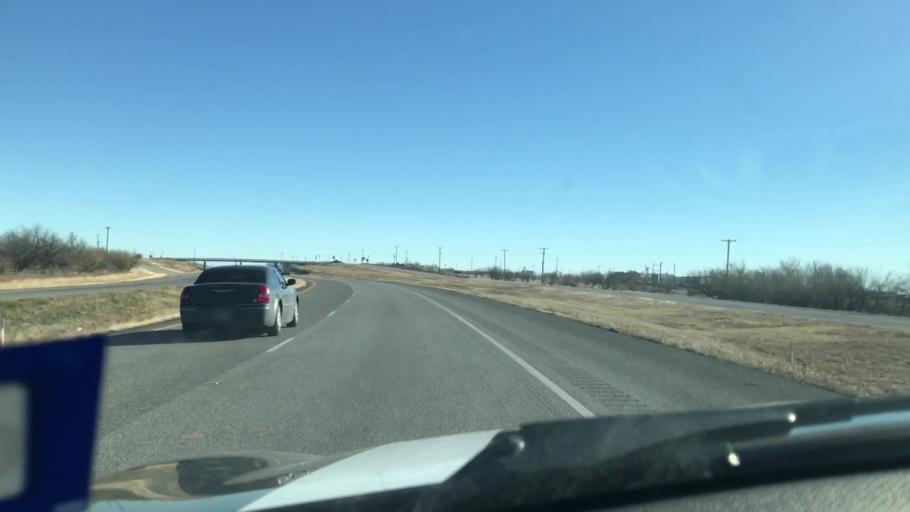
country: US
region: Texas
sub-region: Scurry County
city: Snyder
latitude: 32.7962
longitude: -100.9638
